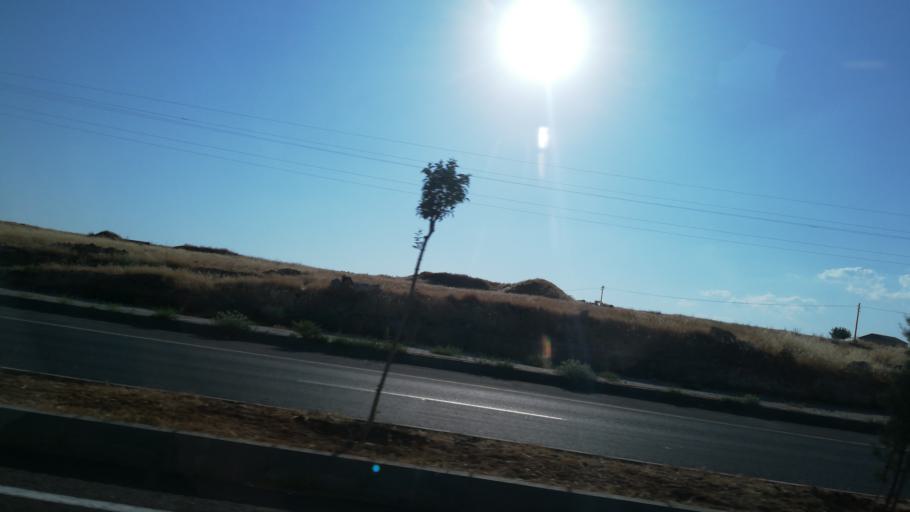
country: TR
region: Mardin
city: Midyat
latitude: 37.4018
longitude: 41.3437
